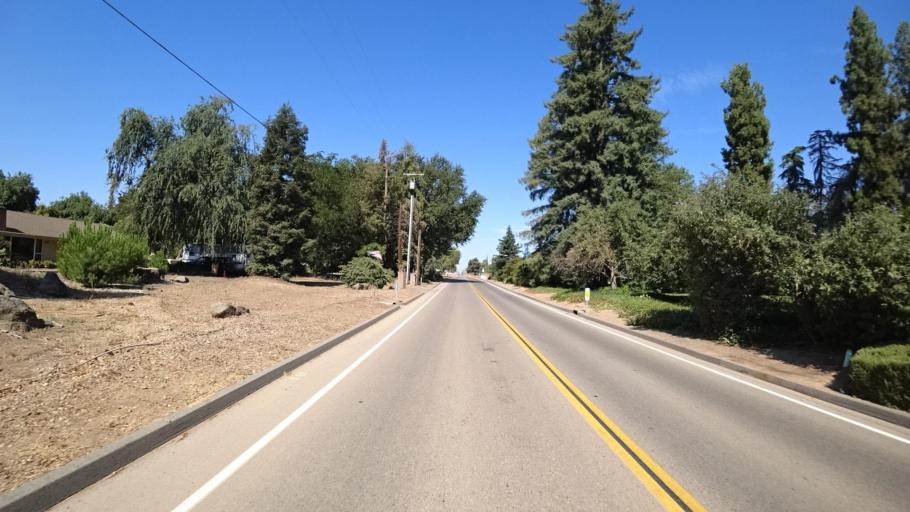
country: US
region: California
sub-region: Fresno County
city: Sunnyside
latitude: 36.7721
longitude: -119.6674
